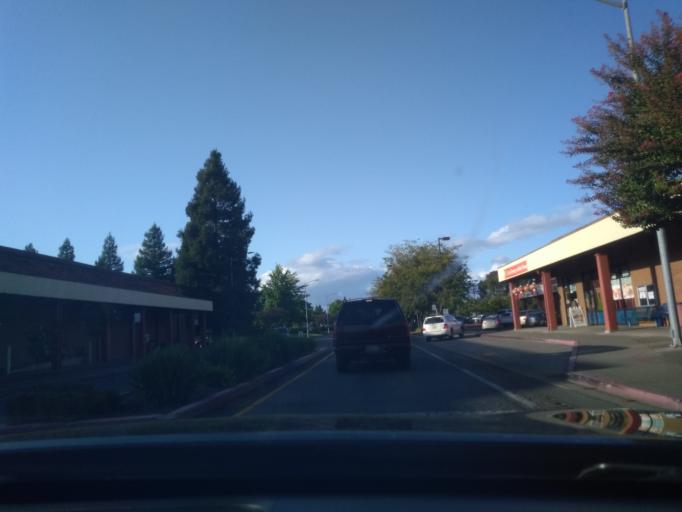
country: US
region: California
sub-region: Mendocino County
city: Ukiah
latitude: 39.1530
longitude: -123.1991
